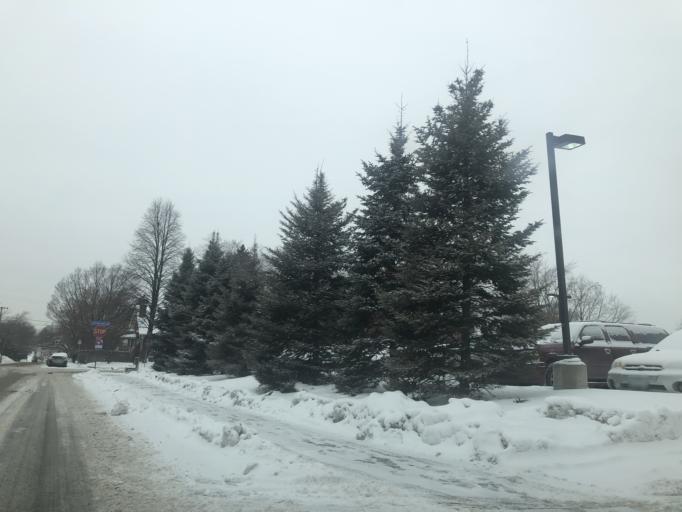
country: US
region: Minnesota
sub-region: Hennepin County
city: Richfield
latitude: 44.9341
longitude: -93.2902
